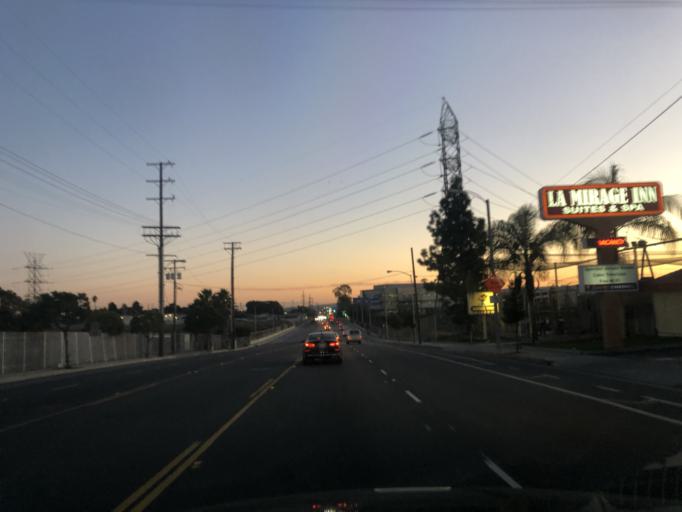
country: US
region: California
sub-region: Los Angeles County
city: West Athens
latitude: 33.9274
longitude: -118.3091
